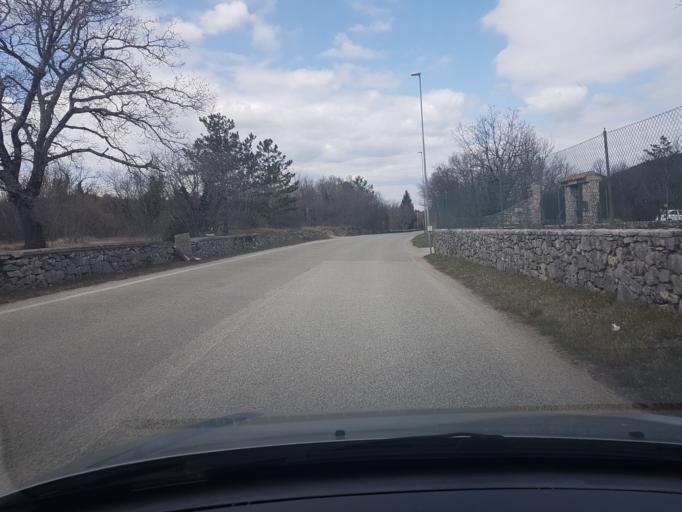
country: IT
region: Friuli Venezia Giulia
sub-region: Provincia di Trieste
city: Santa Croce
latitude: 45.7598
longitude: 13.7062
